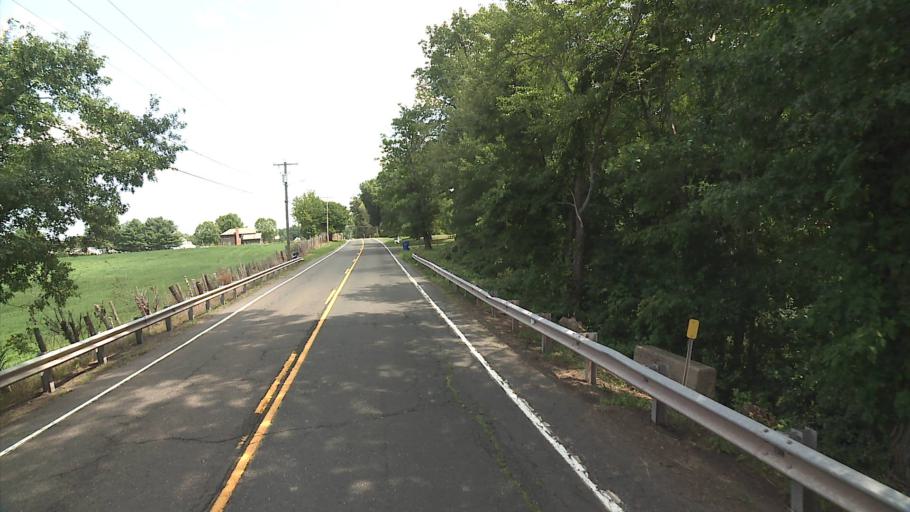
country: US
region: Connecticut
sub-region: Hartford County
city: Windsor Locks
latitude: 41.8961
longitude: -72.5937
